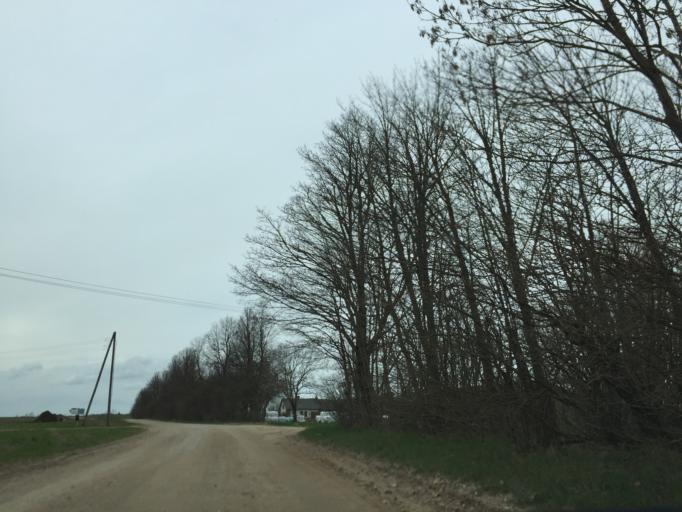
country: LV
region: Priekuli
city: Priekuli
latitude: 57.3396
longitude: 25.3641
